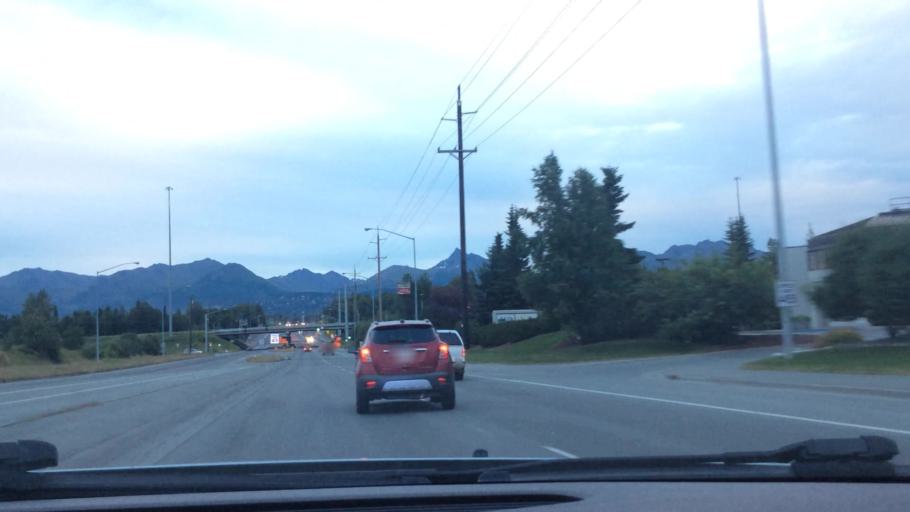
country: US
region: Alaska
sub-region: Anchorage Municipality
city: Anchorage
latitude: 61.1230
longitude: -149.8628
